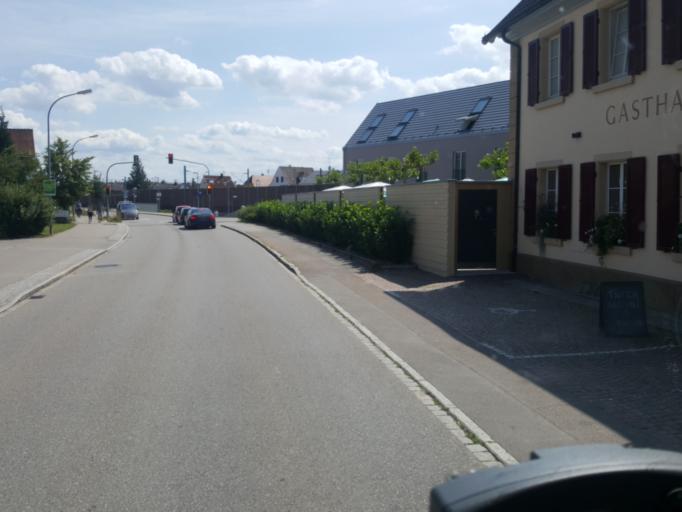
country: DE
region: Baden-Wuerttemberg
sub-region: Freiburg Region
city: Eimeldingen
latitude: 47.6295
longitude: 7.5953
